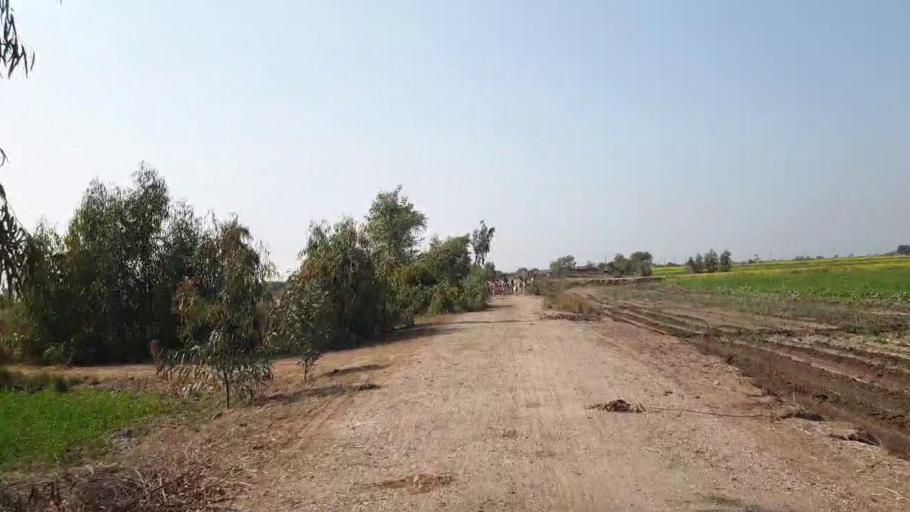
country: PK
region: Sindh
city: Bhit Shah
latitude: 25.9409
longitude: 68.4822
